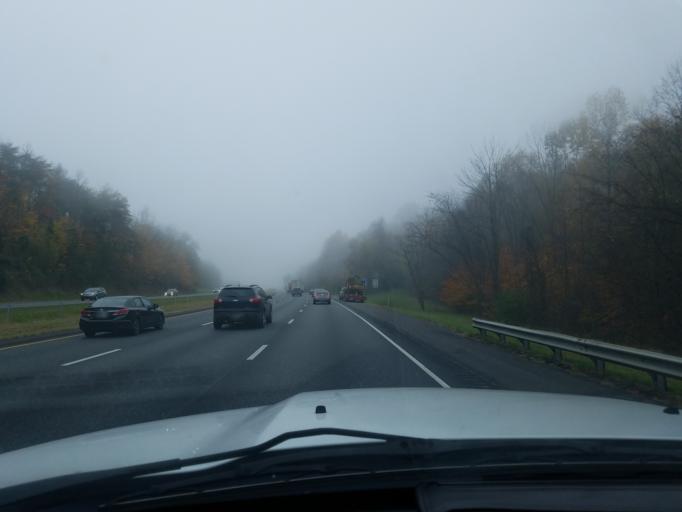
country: US
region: Indiana
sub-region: Floyd County
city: Galena
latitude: 38.3005
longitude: -85.8967
